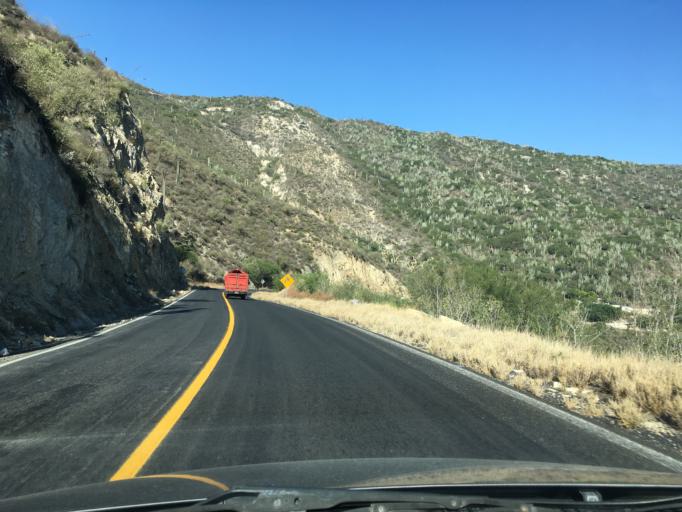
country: MX
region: Hidalgo
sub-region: San Agustin Metzquititlan
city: Mezquititlan
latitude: 20.4671
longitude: -98.6779
